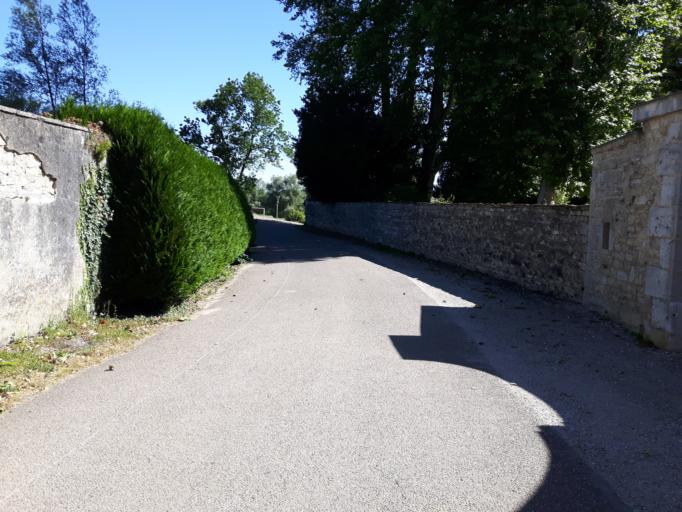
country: FR
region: Franche-Comte
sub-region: Departement du Jura
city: Mouchard
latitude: 47.0141
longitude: 5.8531
